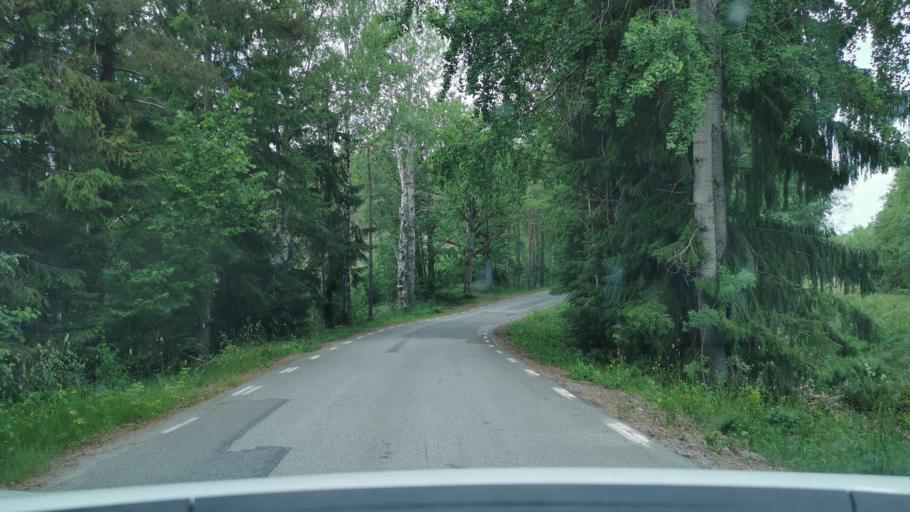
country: SE
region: Vaestra Goetaland
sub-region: Bengtsfors Kommun
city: Dals Langed
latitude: 58.8393
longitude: 12.4099
